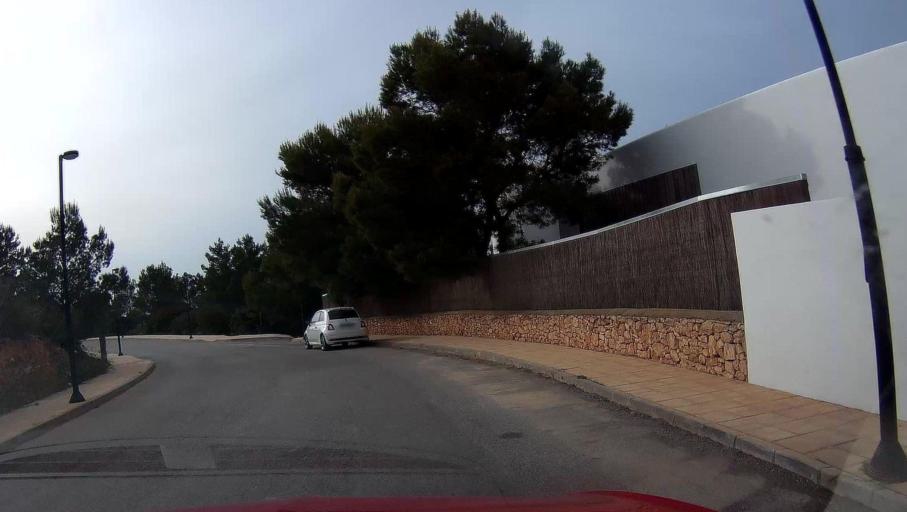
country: ES
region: Balearic Islands
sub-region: Illes Balears
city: Sant Joan de Labritja
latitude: 39.1079
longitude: 1.5120
